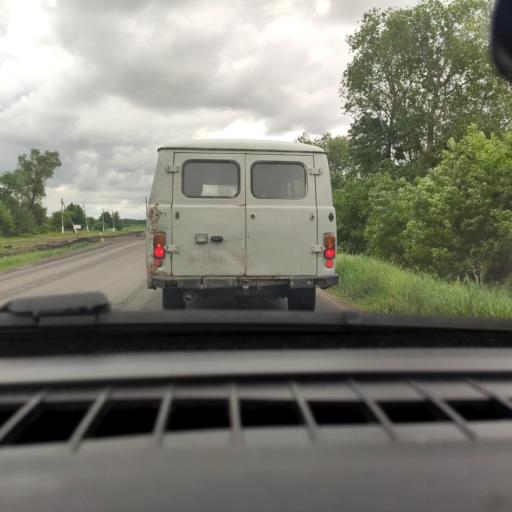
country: RU
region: Lipetsk
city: Usman'
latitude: 51.9433
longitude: 39.7805
